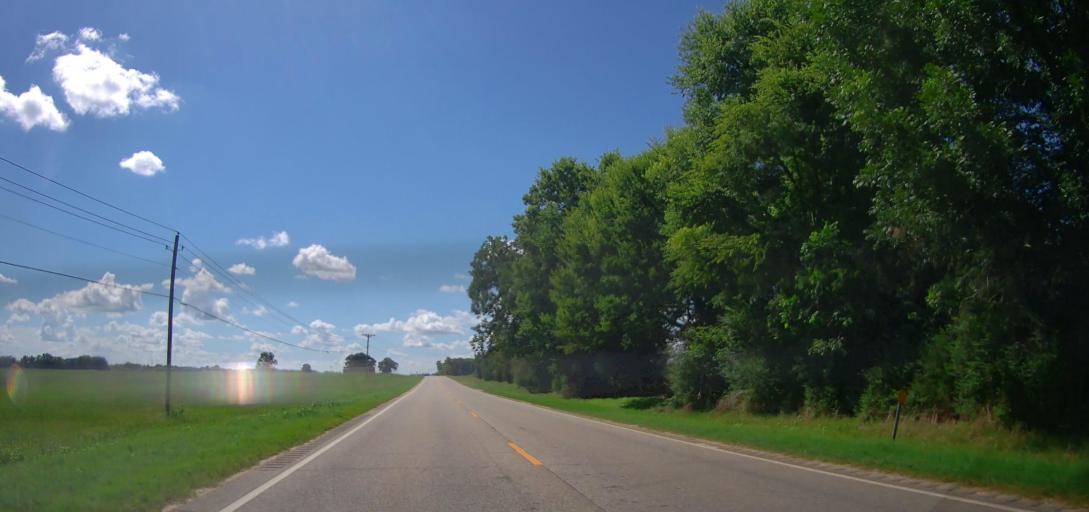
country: US
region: Alabama
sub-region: Elmore County
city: Tallassee
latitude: 32.3838
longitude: -85.8795
